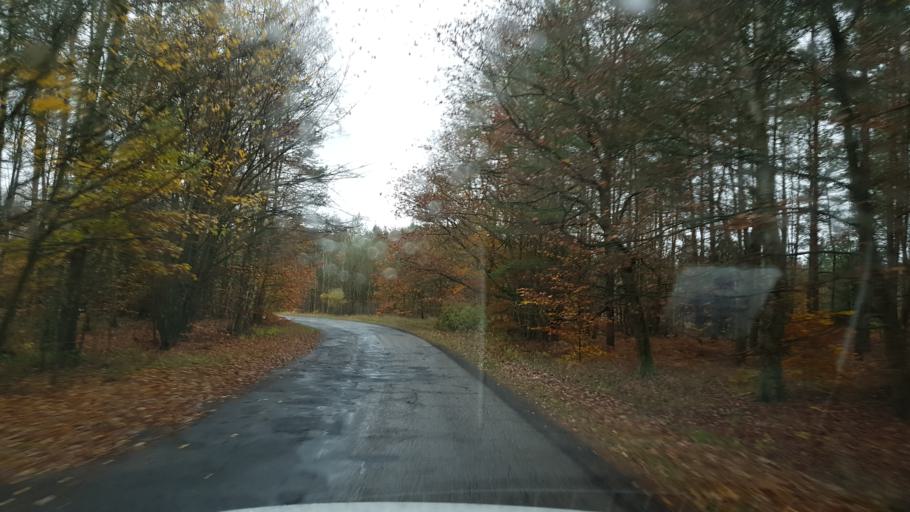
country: PL
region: West Pomeranian Voivodeship
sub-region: Powiat goleniowski
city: Stepnica
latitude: 53.6580
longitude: 14.6885
